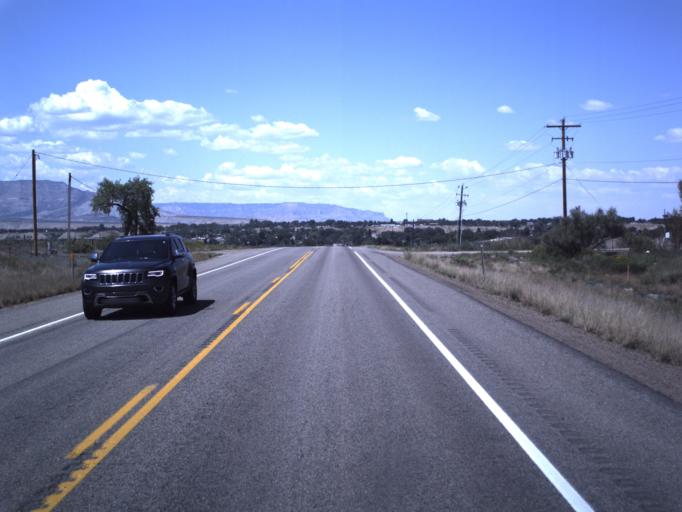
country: US
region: Utah
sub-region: Emery County
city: Castle Dale
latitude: 39.1976
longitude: -111.0241
